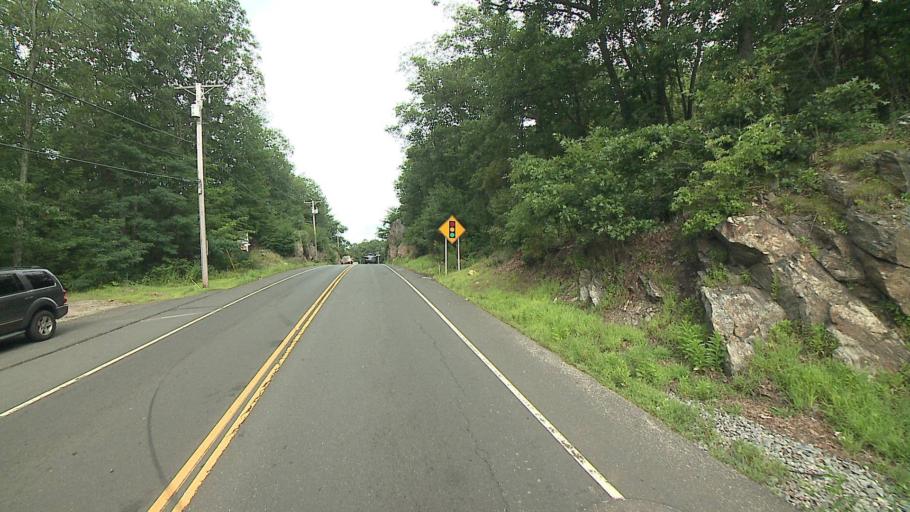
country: US
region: Connecticut
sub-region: New Haven County
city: Waterbury
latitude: 41.5408
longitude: -73.0864
